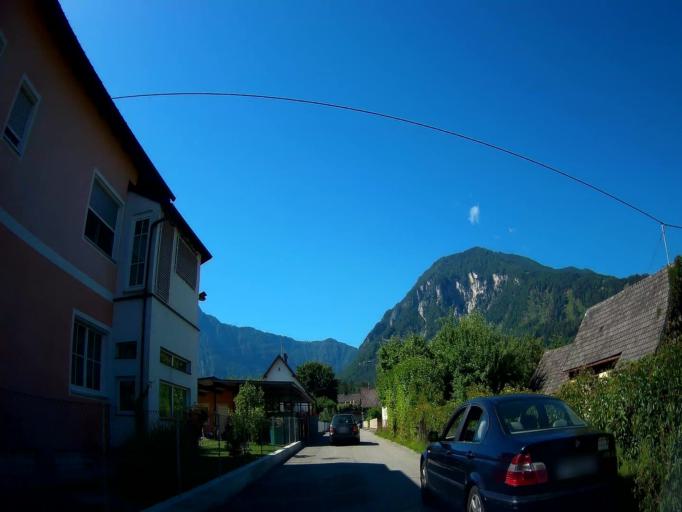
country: AT
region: Carinthia
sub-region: Politischer Bezirk Klagenfurt Land
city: Ferlach
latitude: 46.5256
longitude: 14.2902
